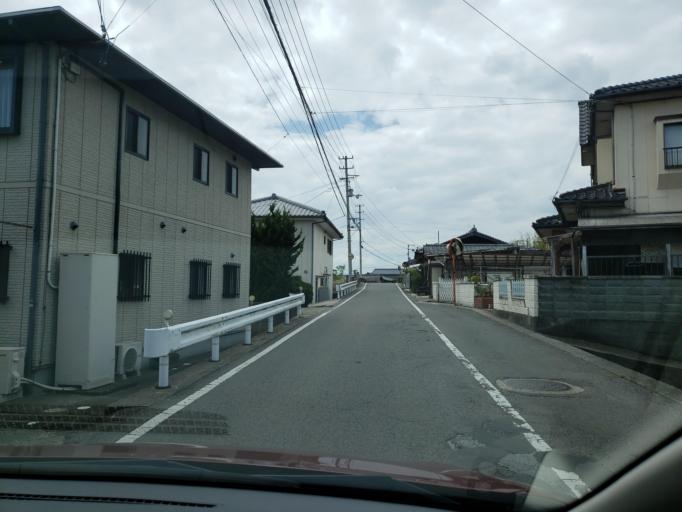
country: JP
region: Tokushima
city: Kamojimacho-jogejima
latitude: 34.0984
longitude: 134.3298
